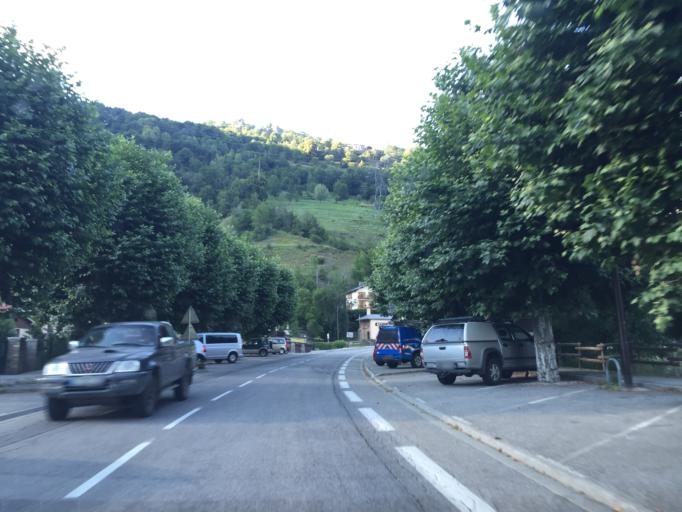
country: FR
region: Rhone-Alpes
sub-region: Departement de la Savoie
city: Bourg-Saint-Maurice
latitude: 45.6219
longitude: 6.7708
